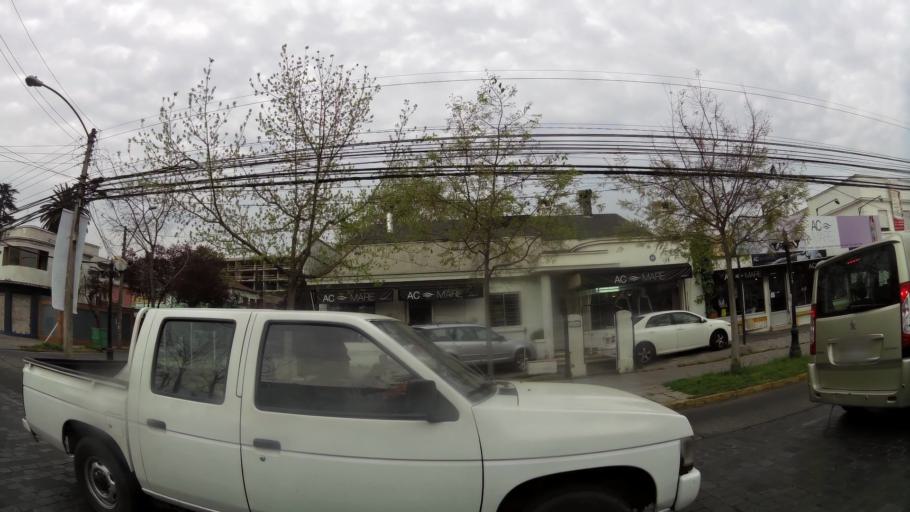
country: CL
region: Santiago Metropolitan
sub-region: Provincia de Santiago
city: Santiago
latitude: -33.4465
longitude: -70.6140
